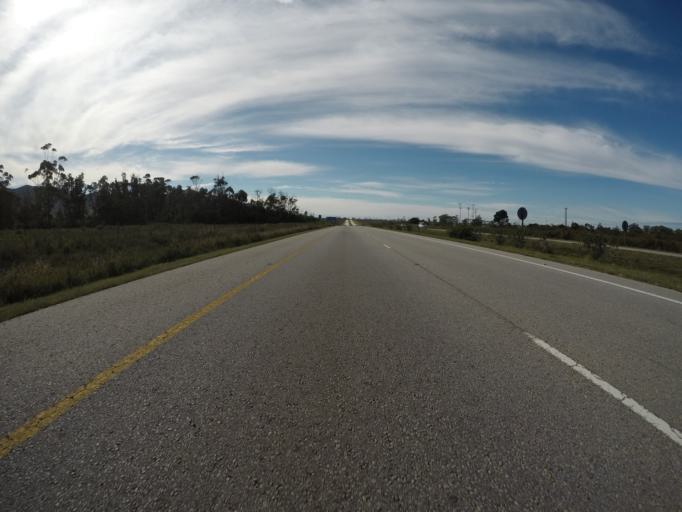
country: ZA
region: Eastern Cape
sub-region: Nelson Mandela Bay Metropolitan Municipality
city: Uitenhage
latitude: -33.9097
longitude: 25.2213
